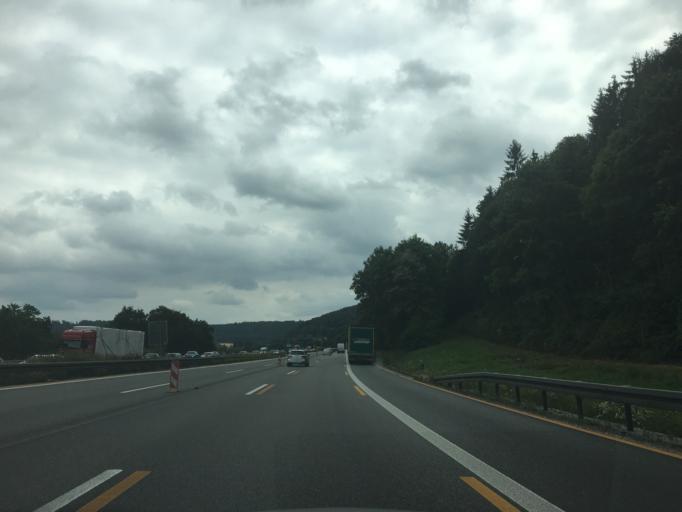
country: DE
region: Bavaria
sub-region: Regierungsbezirk Mittelfranken
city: Greding
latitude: 49.0374
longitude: 11.3583
